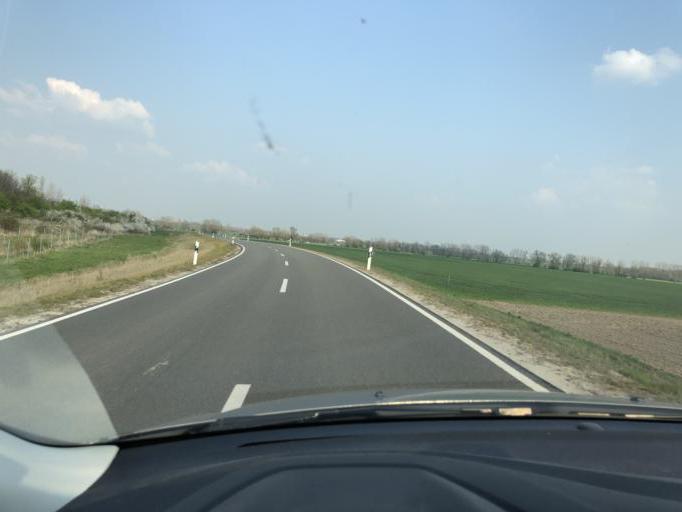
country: DE
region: Saxony
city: Rackwitz
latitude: 51.4277
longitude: 12.3298
